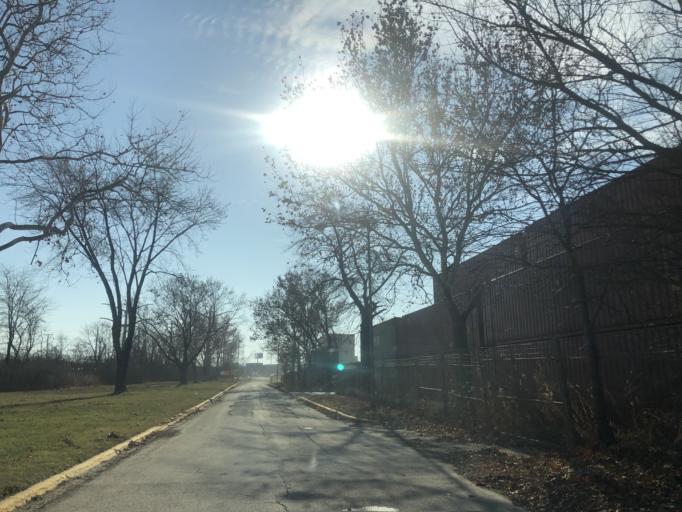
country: US
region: Illinois
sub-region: Cook County
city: Stickney
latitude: 41.8130
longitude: -87.7831
